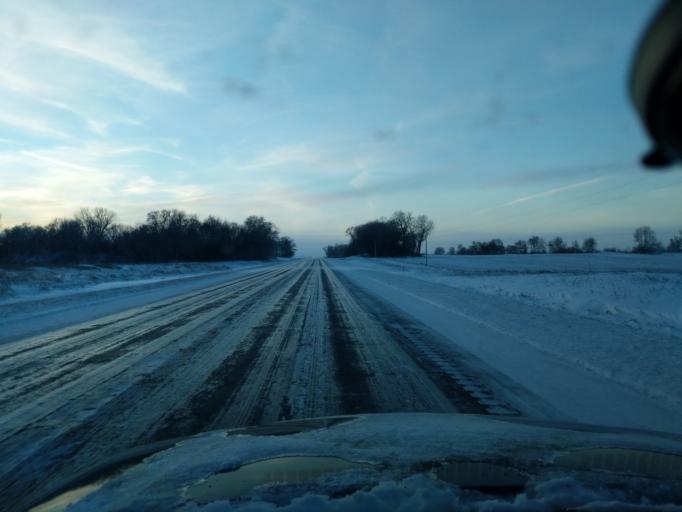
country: US
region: Minnesota
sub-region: Renville County
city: Renville
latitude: 44.7890
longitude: -95.2831
